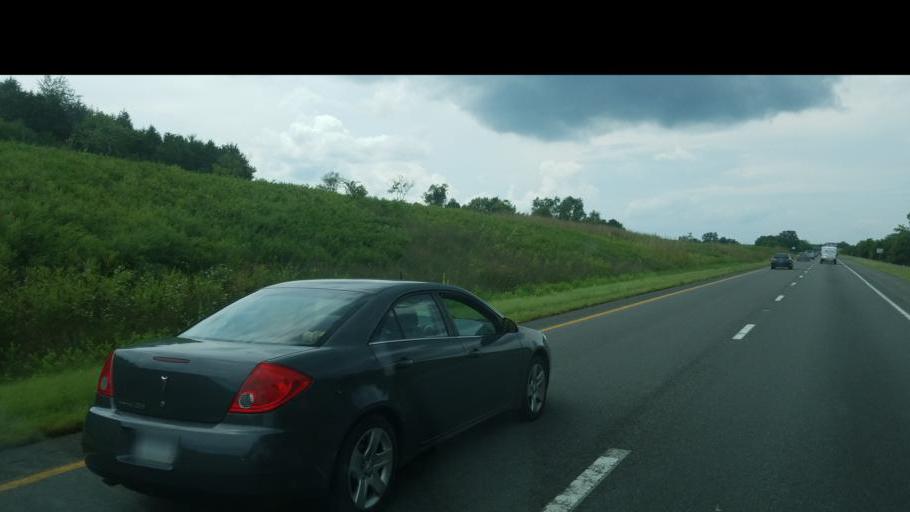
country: US
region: Virginia
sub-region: Warren County
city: Apple Mountain Lake
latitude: 38.9420
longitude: -78.1357
